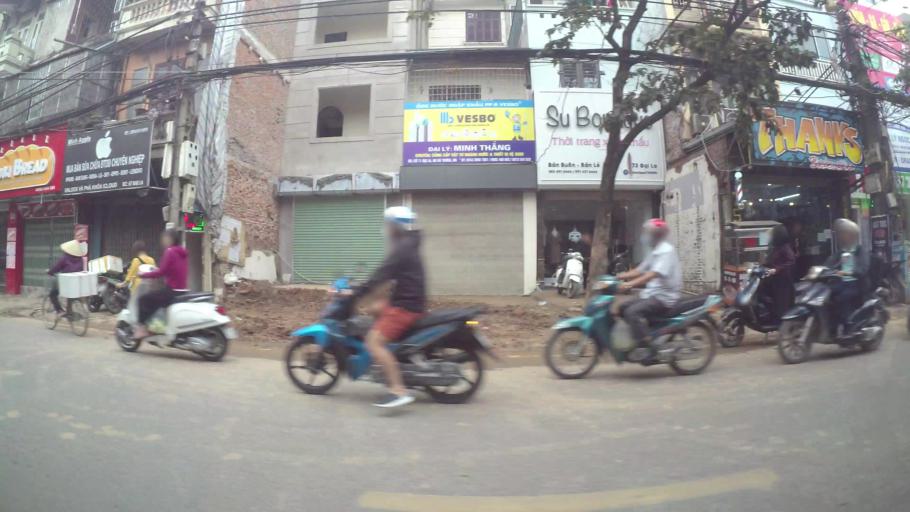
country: VN
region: Ha Noi
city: Hai BaTrung
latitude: 20.9961
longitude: 105.8482
